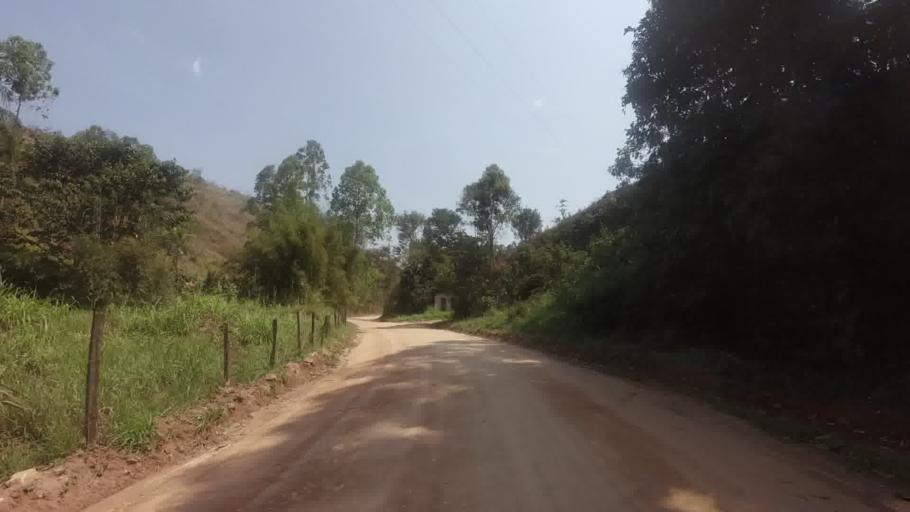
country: BR
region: Espirito Santo
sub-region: Mimoso Do Sul
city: Mimoso do Sul
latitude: -20.9440
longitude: -41.4036
